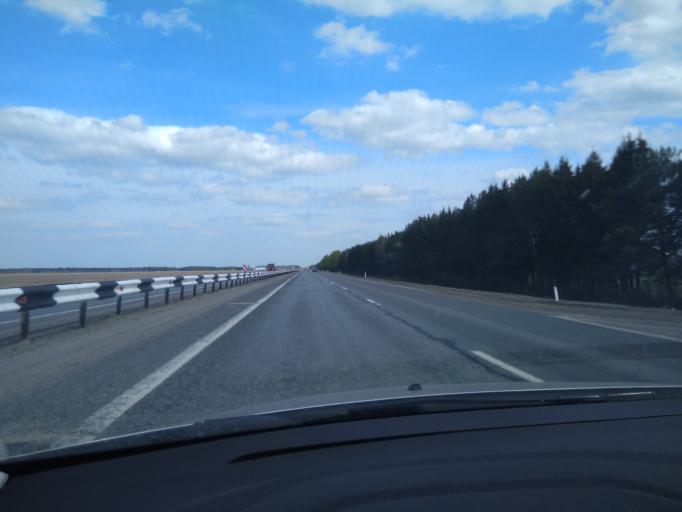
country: RU
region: Tjumen
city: Moskovskiy
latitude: 57.0948
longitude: 65.1844
